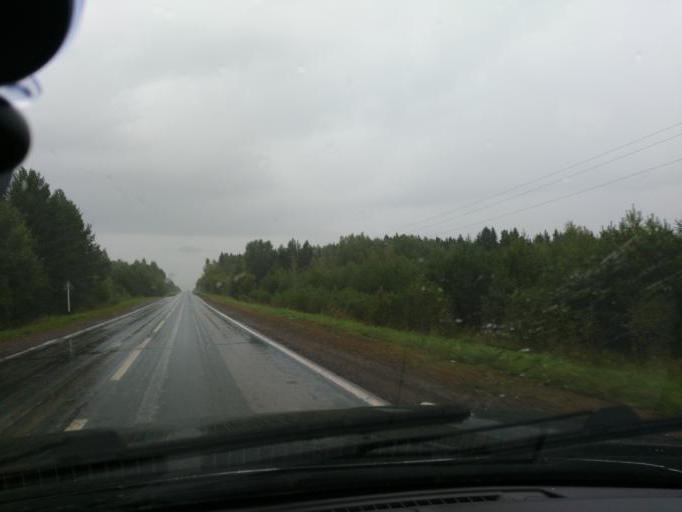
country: RU
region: Perm
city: Osa
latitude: 57.1211
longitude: 55.5234
